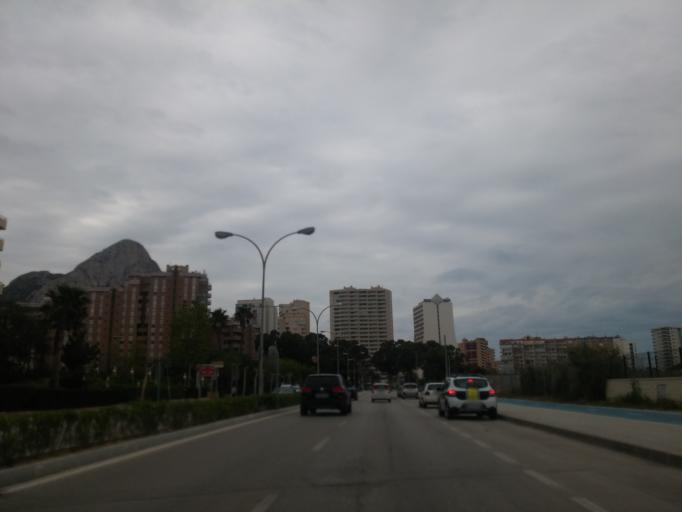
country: ES
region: Valencia
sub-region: Provincia de Alicante
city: Calp
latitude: 38.6462
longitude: 0.0713
